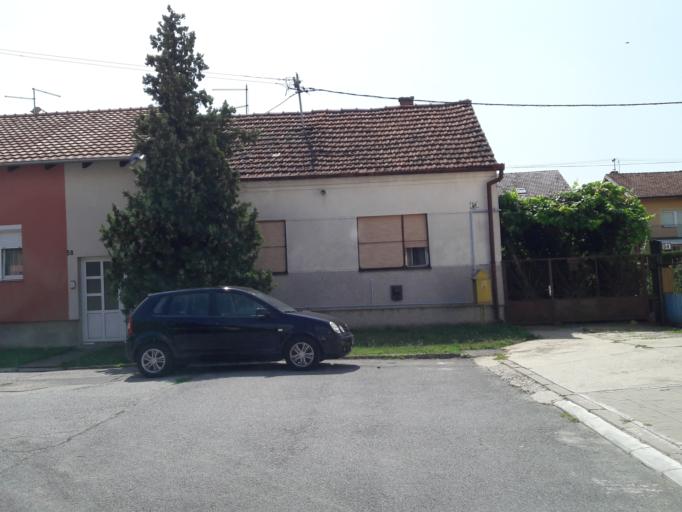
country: HR
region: Osjecko-Baranjska
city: Visnjevac
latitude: 45.5586
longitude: 18.6452
